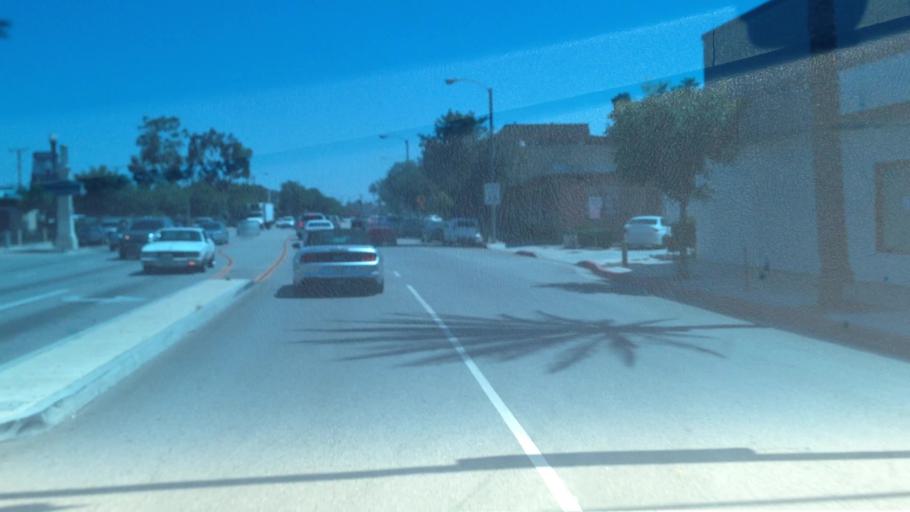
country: US
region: California
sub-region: Los Angeles County
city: Montebello
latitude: 34.0100
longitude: -118.1084
